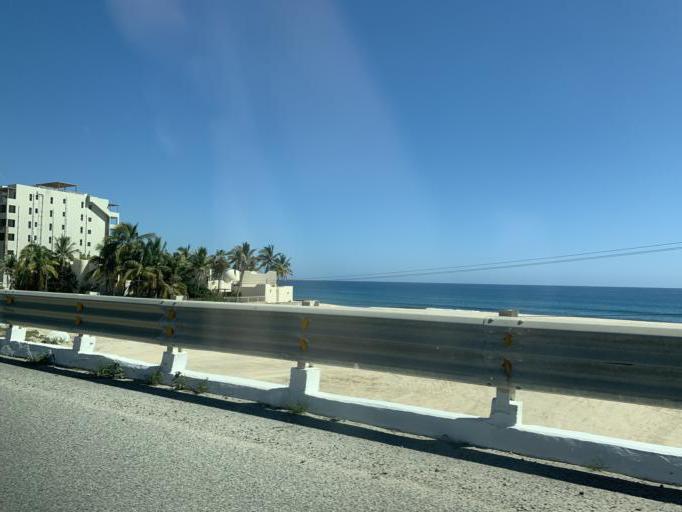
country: MX
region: Baja California Sur
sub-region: Los Cabos
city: San Jose del Cabo
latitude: 23.0291
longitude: -109.7159
